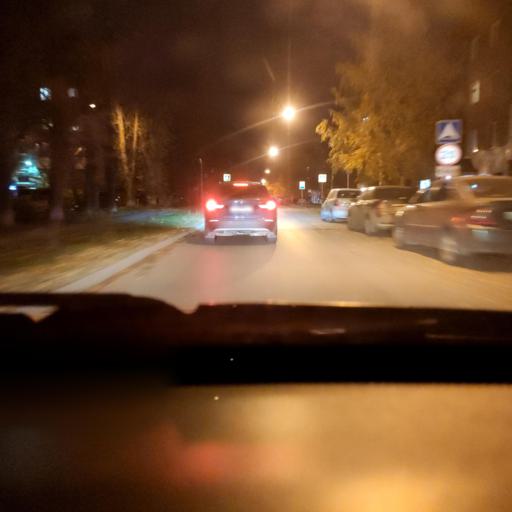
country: RU
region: Perm
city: Kondratovo
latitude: 57.9768
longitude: 56.1711
